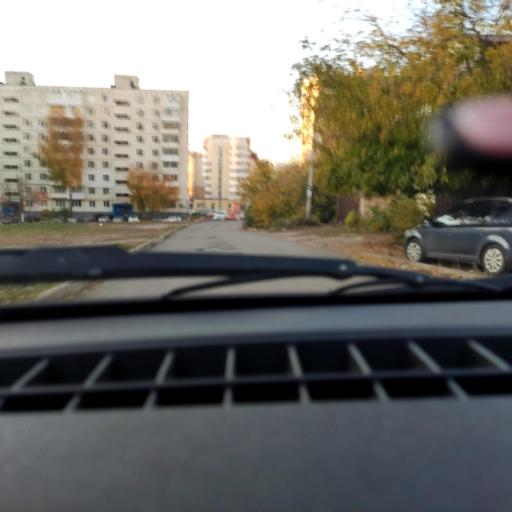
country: RU
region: Bashkortostan
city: Ufa
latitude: 54.7002
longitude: 55.9877
